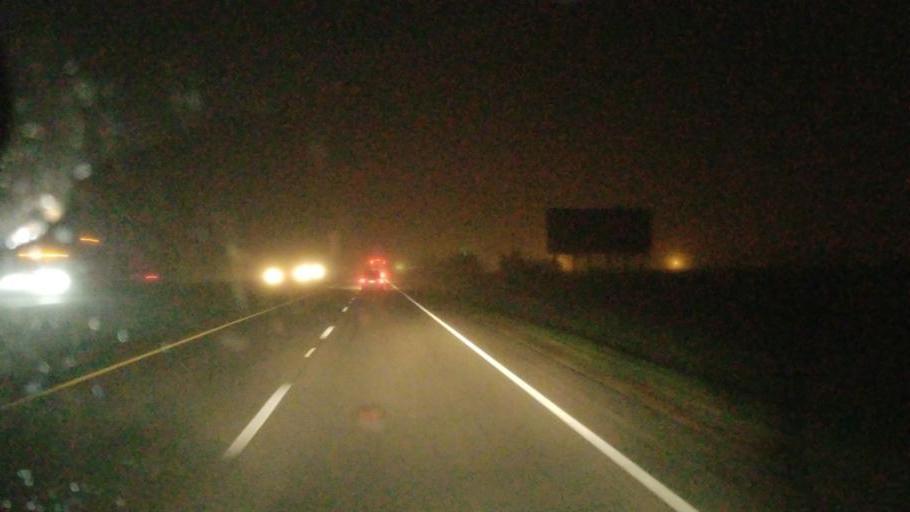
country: US
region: Ohio
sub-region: Pickaway County
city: Circleville
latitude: 39.6335
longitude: -82.9557
